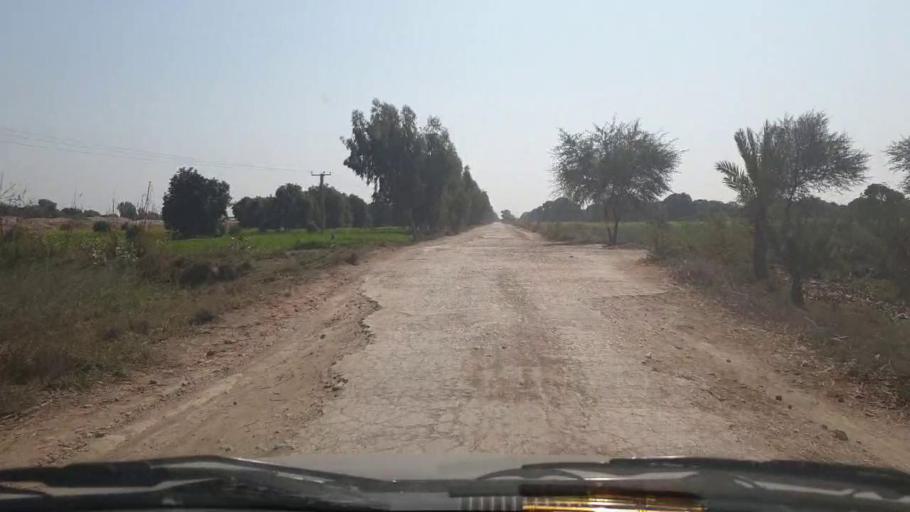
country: PK
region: Sindh
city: Samaro
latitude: 25.2698
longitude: 69.3463
